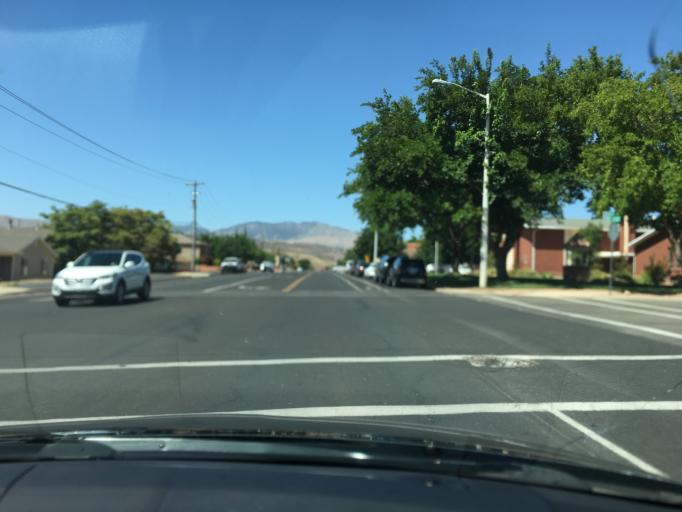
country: US
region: Utah
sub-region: Washington County
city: Ivins
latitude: 37.1684
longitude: -113.6794
